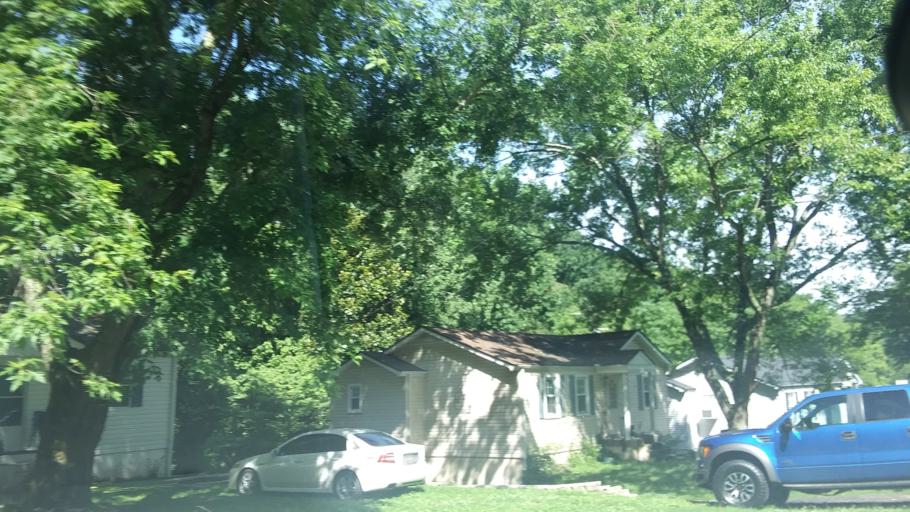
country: US
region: Tennessee
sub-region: Rutherford County
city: La Vergne
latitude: 36.0698
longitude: -86.6683
